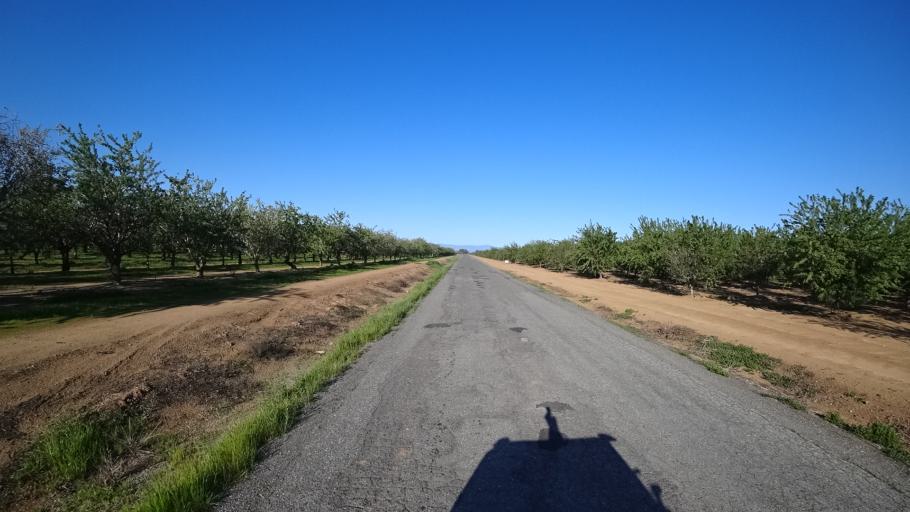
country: US
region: California
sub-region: Glenn County
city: Orland
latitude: 39.7975
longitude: -122.1261
